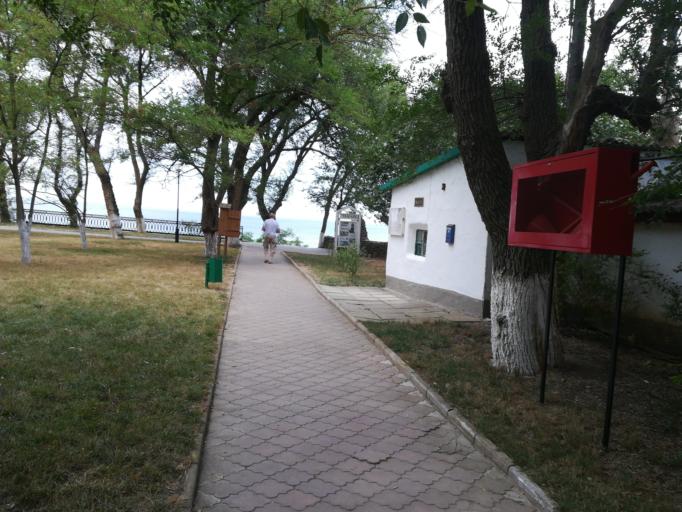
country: RU
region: Krasnodarskiy
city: Taman'
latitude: 45.2178
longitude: 36.7252
